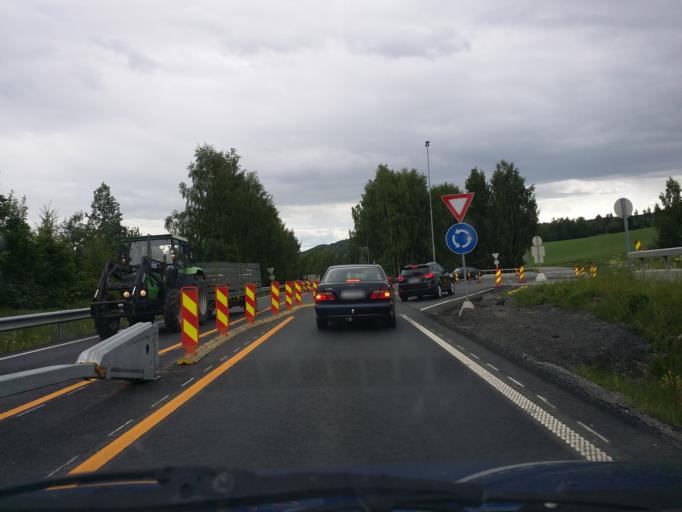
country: NO
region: Hedmark
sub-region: Ringsaker
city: Moelv
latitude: 60.9713
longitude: 10.5960
